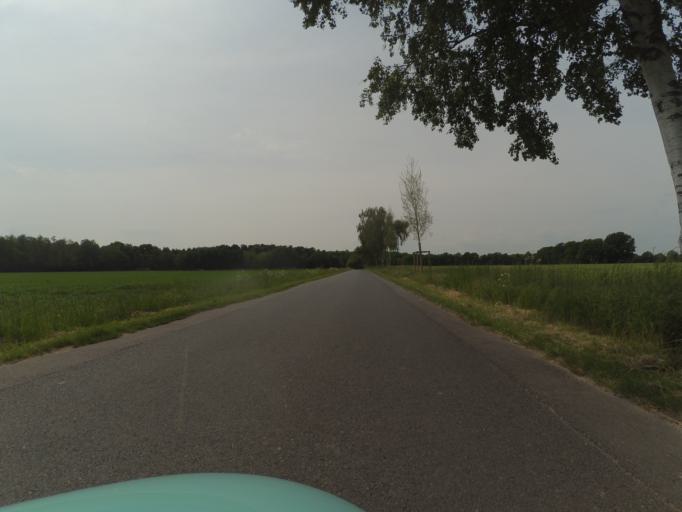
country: DE
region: Lower Saxony
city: Arpke
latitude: 52.3531
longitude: 10.1351
